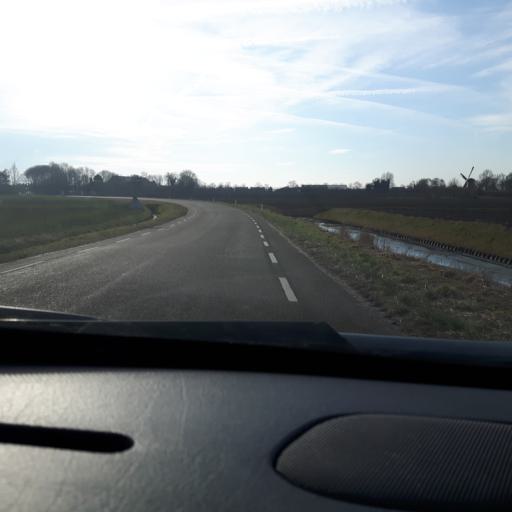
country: NL
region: Zeeland
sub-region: Gemeente Goes
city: Goes
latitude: 51.4303
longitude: 3.9084
